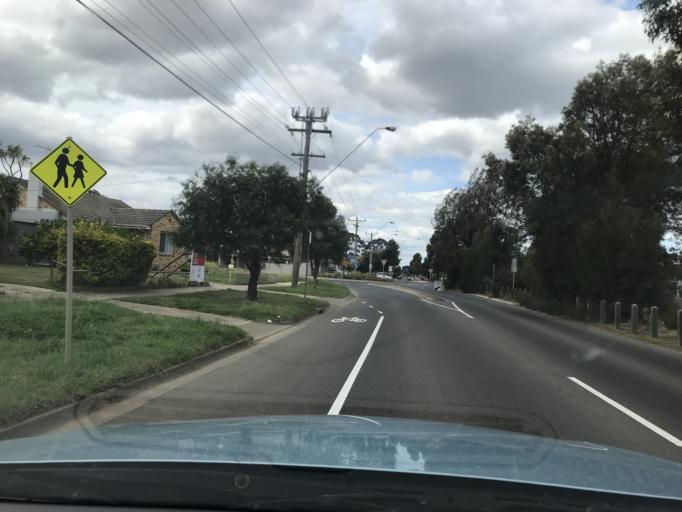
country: AU
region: Victoria
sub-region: Hobsons Bay
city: Laverton
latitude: -37.8641
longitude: 144.7687
